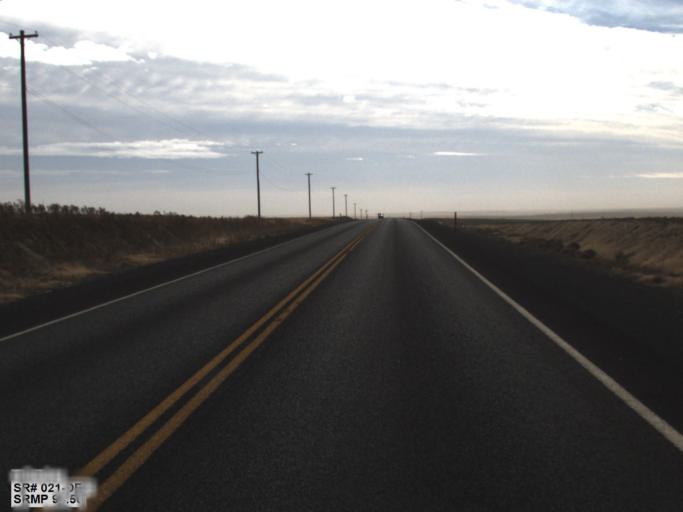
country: US
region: Washington
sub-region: Okanogan County
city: Coulee Dam
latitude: 47.7930
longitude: -118.7218
